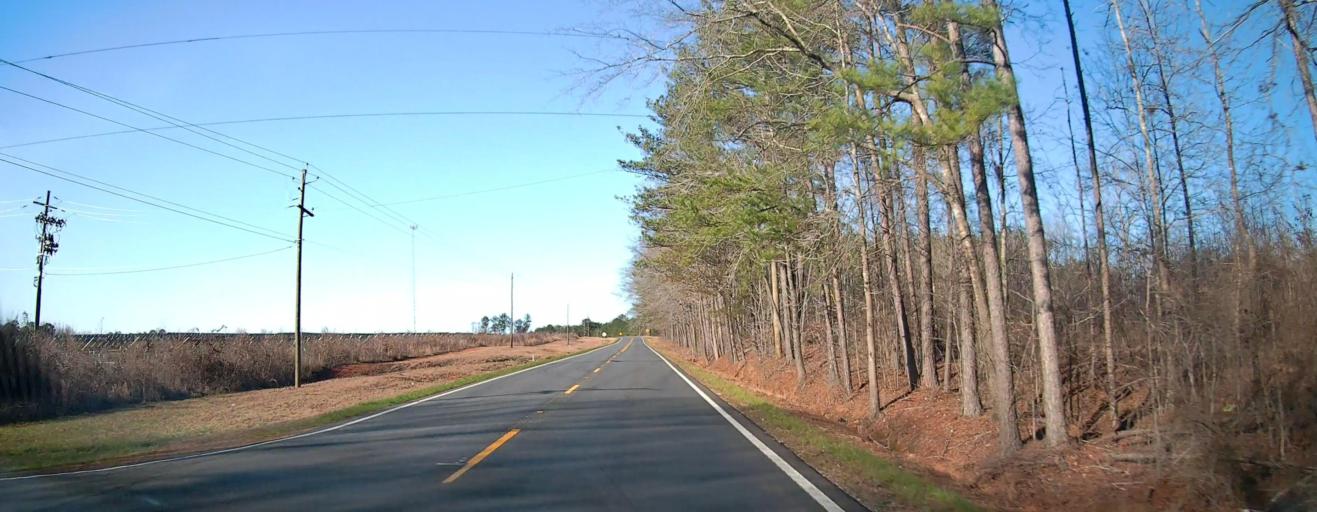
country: US
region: Georgia
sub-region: Talbot County
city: Sardis
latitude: 32.7937
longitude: -84.6927
